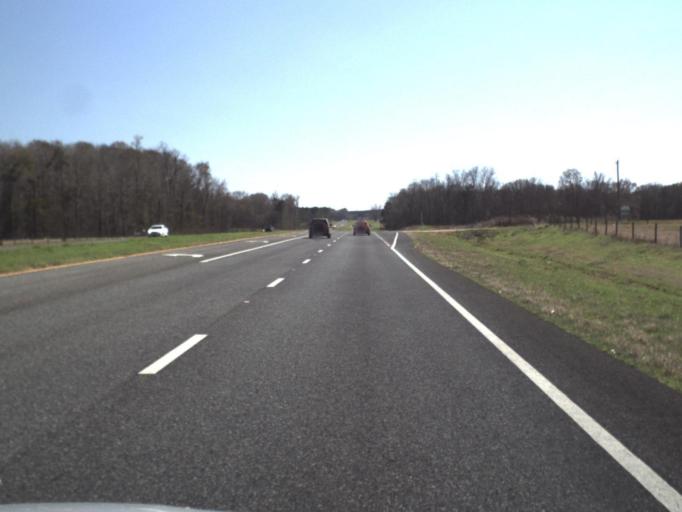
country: US
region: Florida
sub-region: Jackson County
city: Marianna
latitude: 30.8594
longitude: -85.3544
